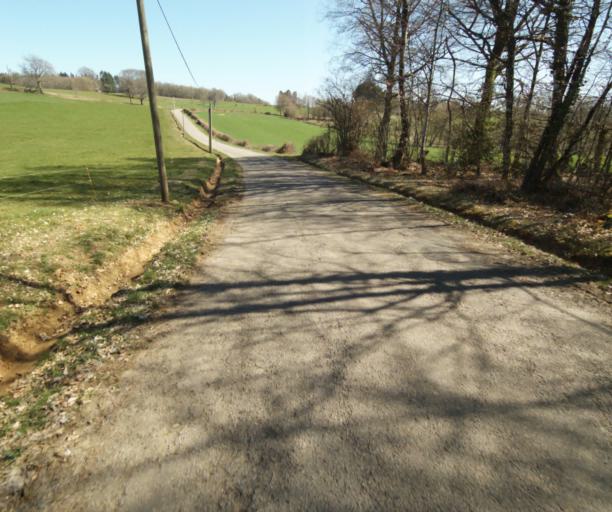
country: FR
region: Limousin
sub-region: Departement de la Correze
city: Saint-Clement
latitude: 45.3068
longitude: 1.7102
